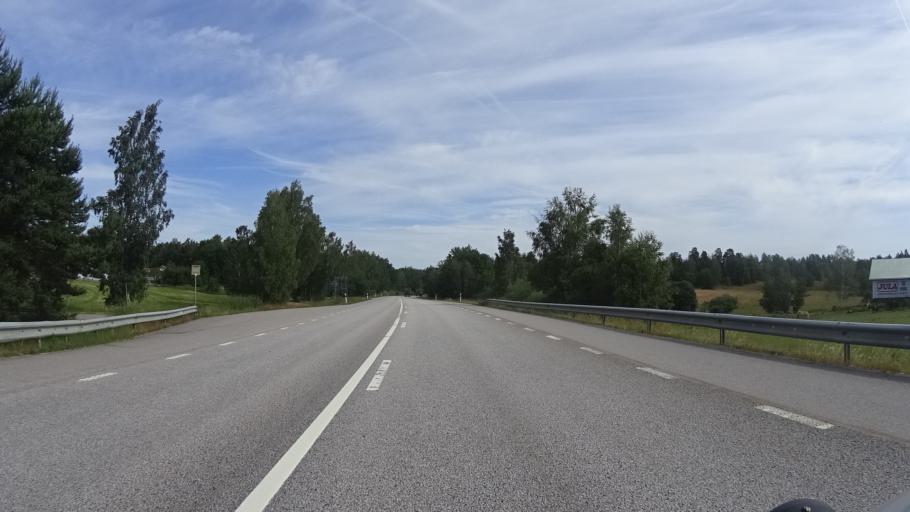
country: SE
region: Kalmar
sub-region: Vasterviks Kommun
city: Ankarsrum
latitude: 57.7144
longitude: 16.4503
